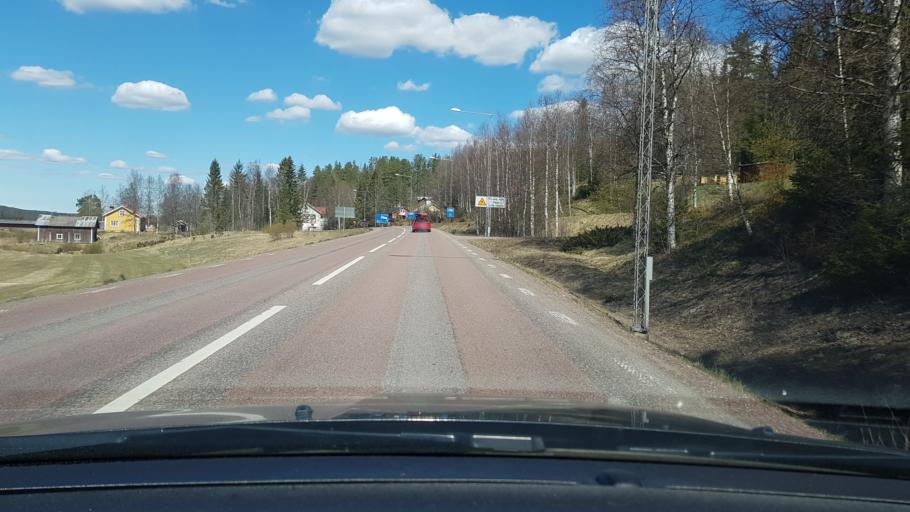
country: SE
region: Dalarna
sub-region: Malung-Saelens kommun
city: Malung
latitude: 61.1459
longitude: 13.2749
